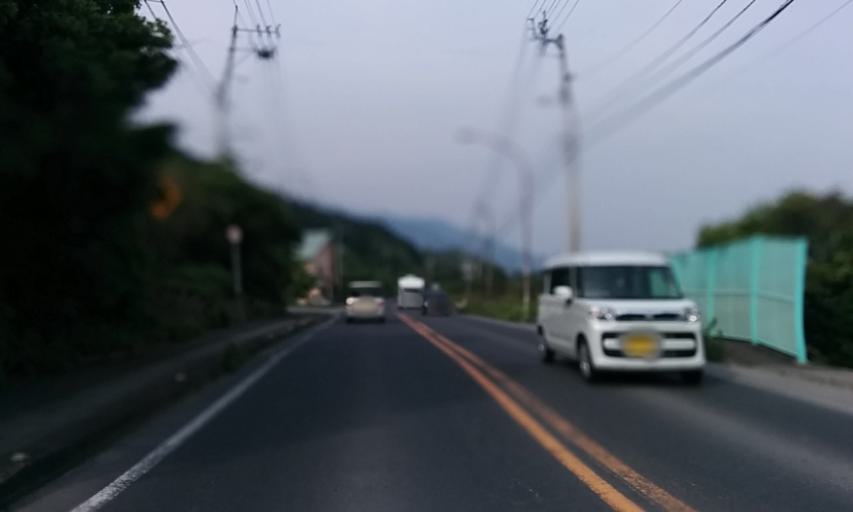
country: JP
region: Ehime
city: Niihama
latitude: 33.9596
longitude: 133.4434
